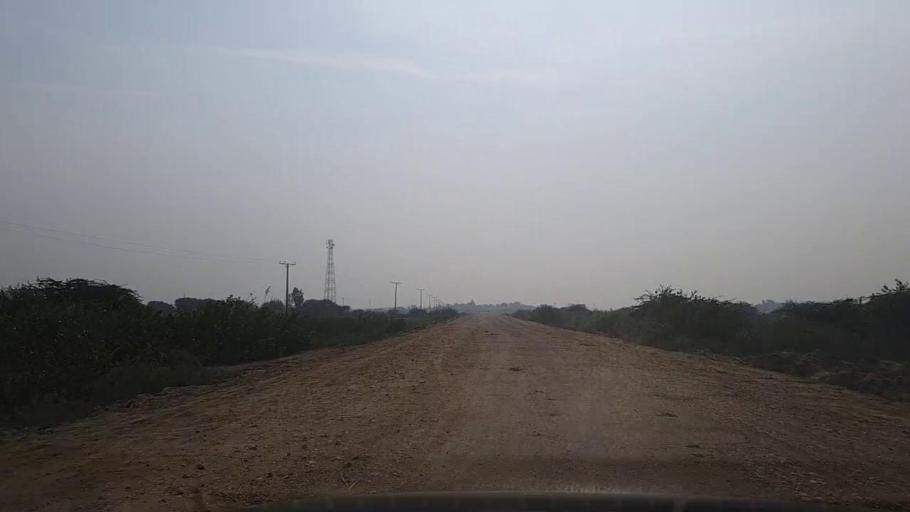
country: PK
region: Sindh
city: Mirpur Sakro
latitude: 24.4085
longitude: 67.7442
